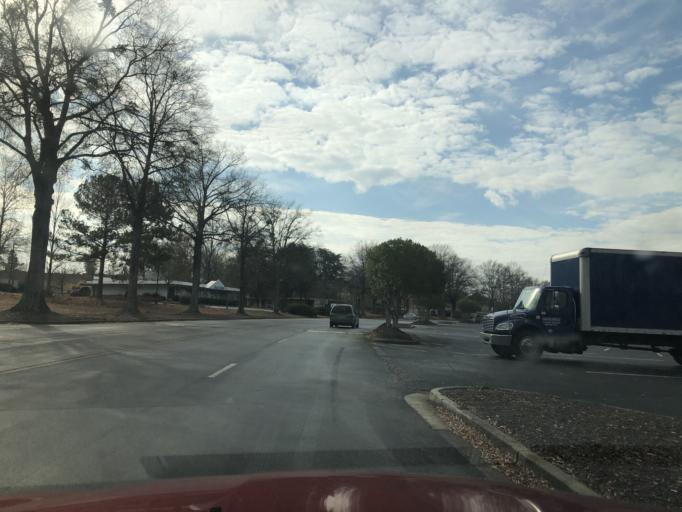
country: US
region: Georgia
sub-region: Clayton County
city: Morrow
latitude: 33.5752
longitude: -84.3483
